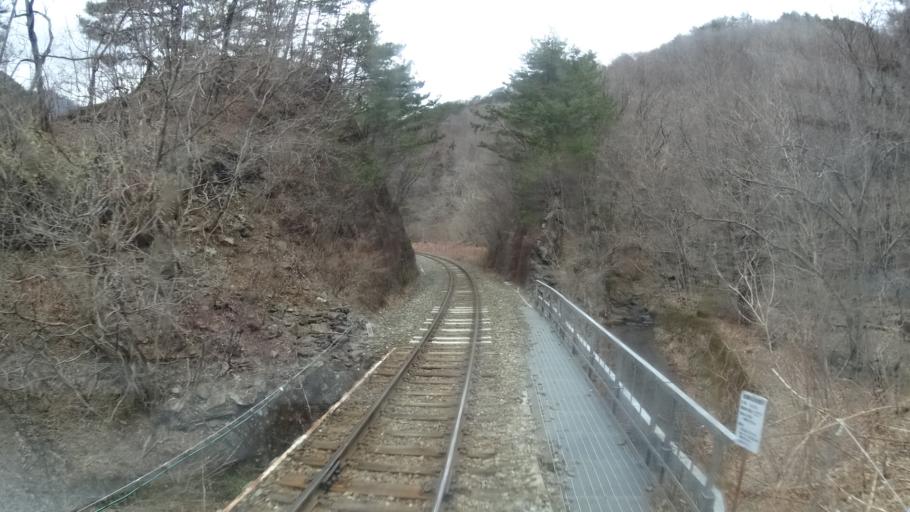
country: JP
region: Iwate
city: Kamaishi
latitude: 39.2735
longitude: 141.7250
